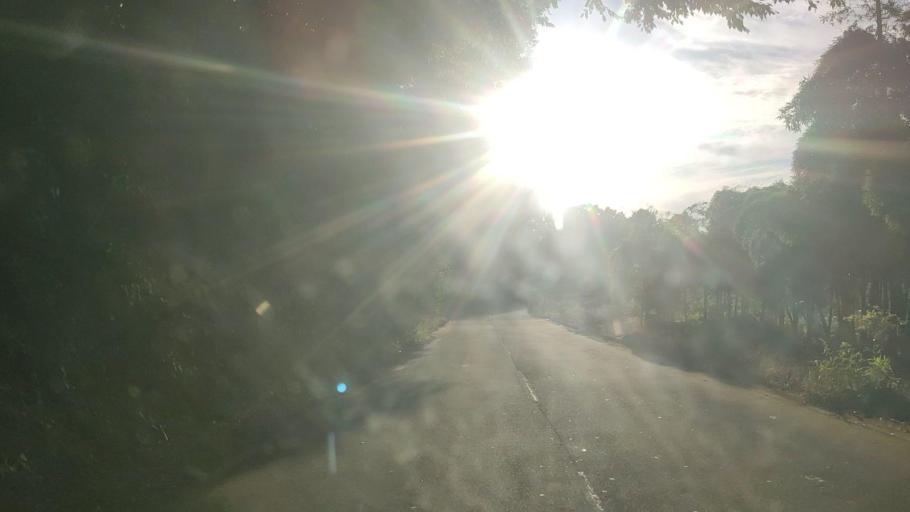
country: JP
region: Shizuoka
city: Mishima
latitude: 35.1503
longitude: 138.9397
